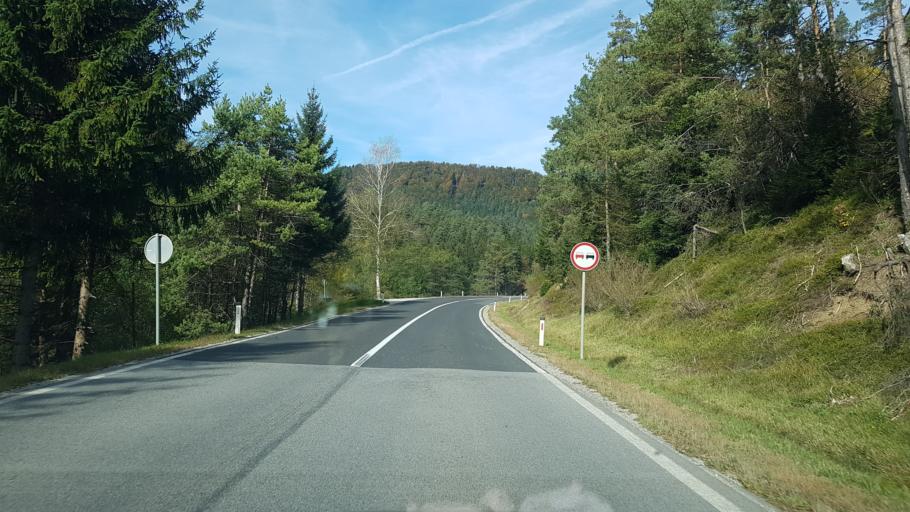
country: SI
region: Mislinja
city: Mislinja
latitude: 46.4309
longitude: 15.1901
